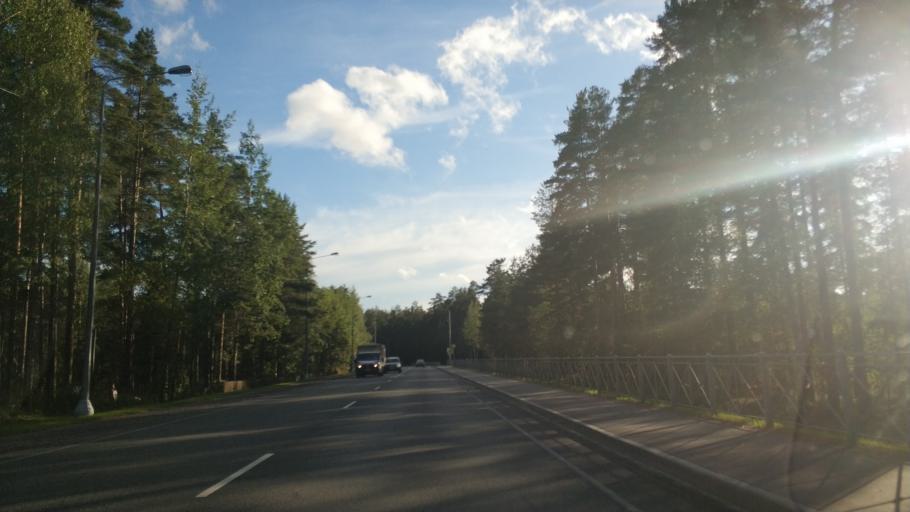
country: RU
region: Leningrad
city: Sapernoye
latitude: 60.7093
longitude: 29.9714
